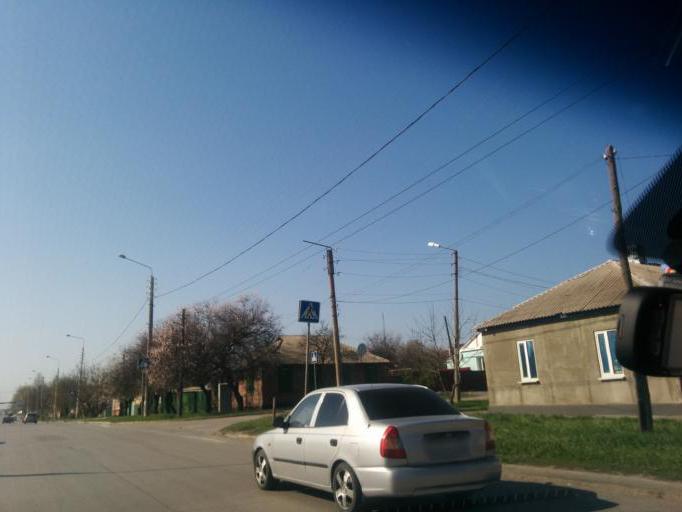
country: RU
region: Rostov
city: Shakhty
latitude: 47.7010
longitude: 40.2029
